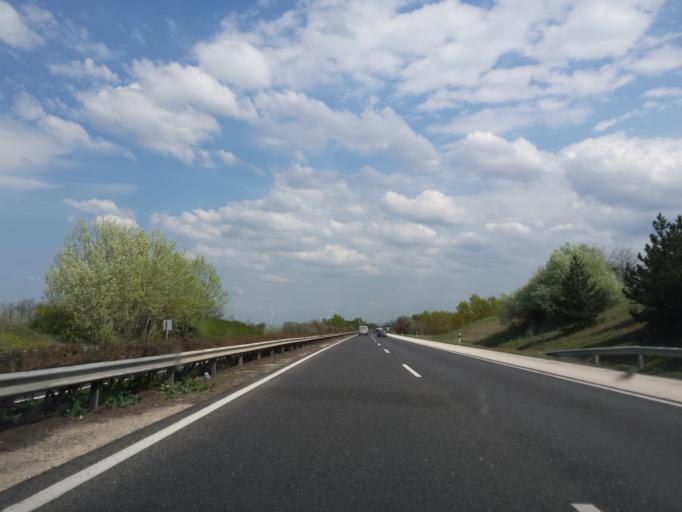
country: HU
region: Komarom-Esztergom
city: Acs
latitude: 47.6824
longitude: 18.0203
